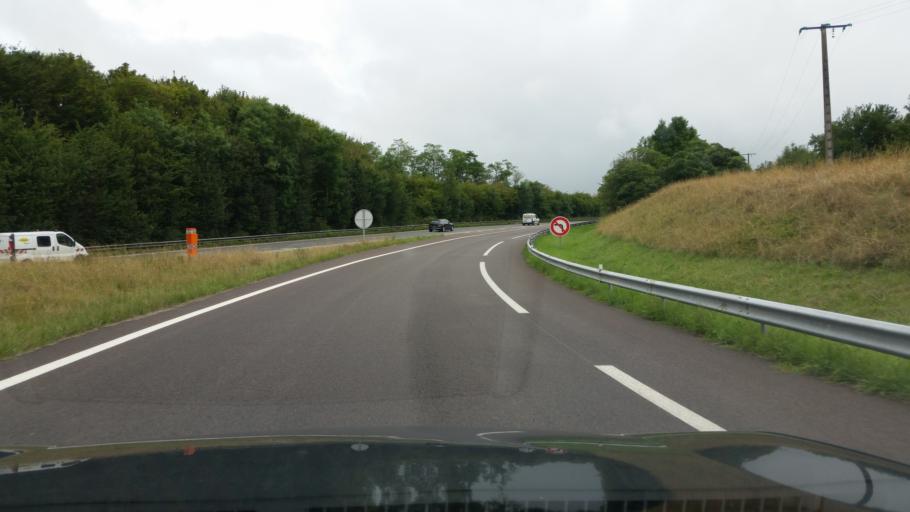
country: FR
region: Lorraine
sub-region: Departement de Meurthe-et-Moselle
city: Dommartin-les-Toul
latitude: 48.6524
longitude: 5.8800
